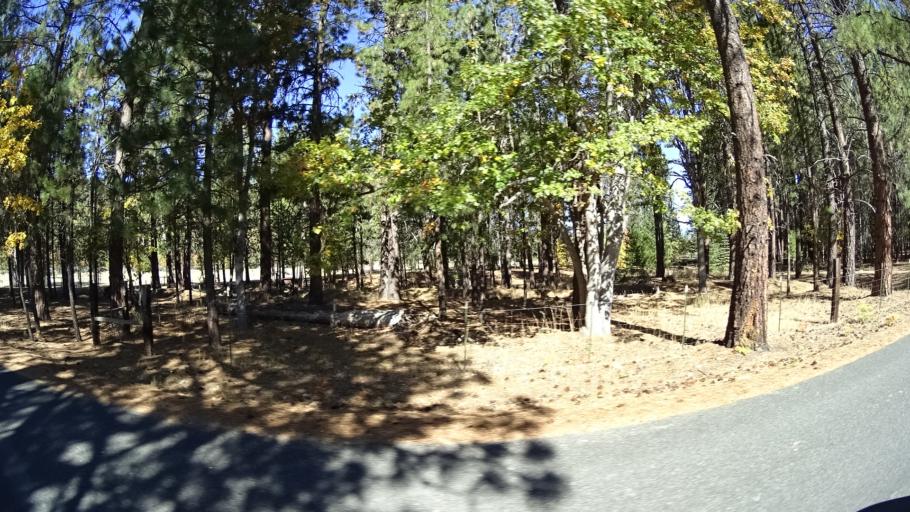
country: US
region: California
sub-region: Siskiyou County
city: Yreka
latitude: 41.5485
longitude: -122.9343
